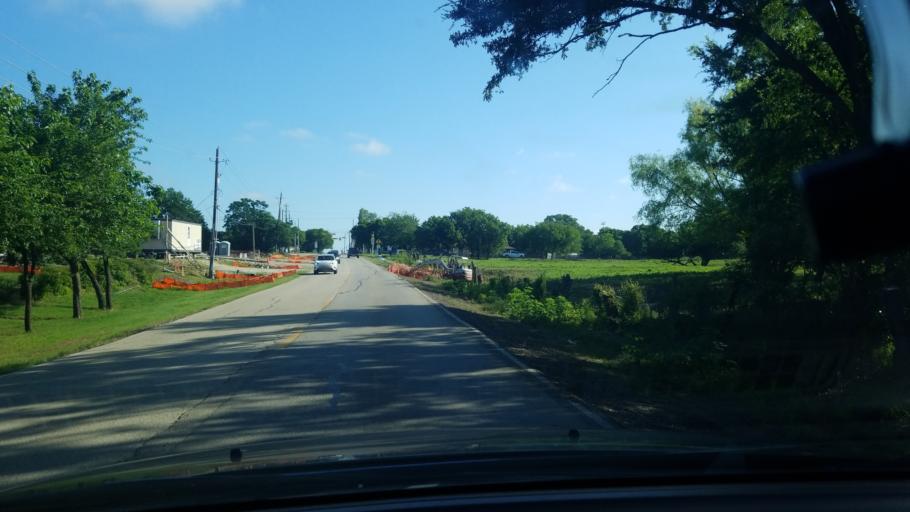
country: US
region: Texas
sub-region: Dallas County
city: Sunnyvale
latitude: 32.7915
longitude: -96.5612
